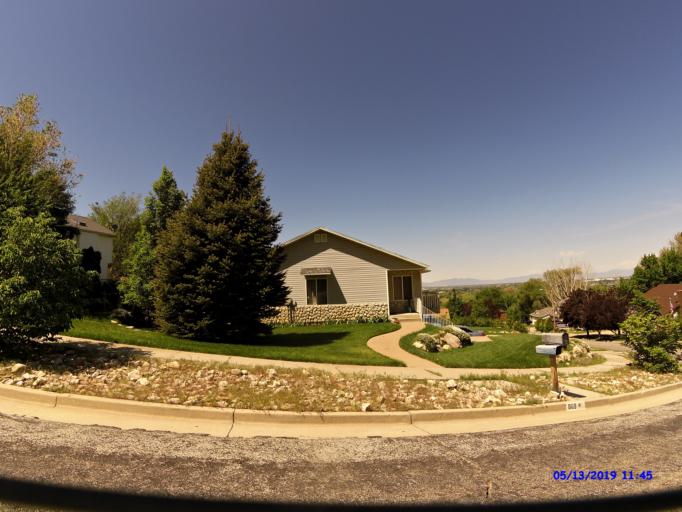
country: US
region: Utah
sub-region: Weber County
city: North Ogden
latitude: 41.2734
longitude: -111.9482
